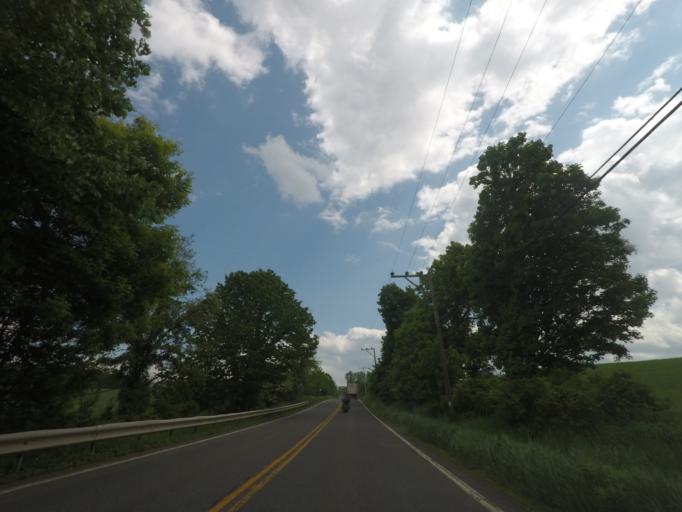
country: US
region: New York
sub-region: Dutchess County
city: Pine Plains
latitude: 42.0403
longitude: -73.6163
